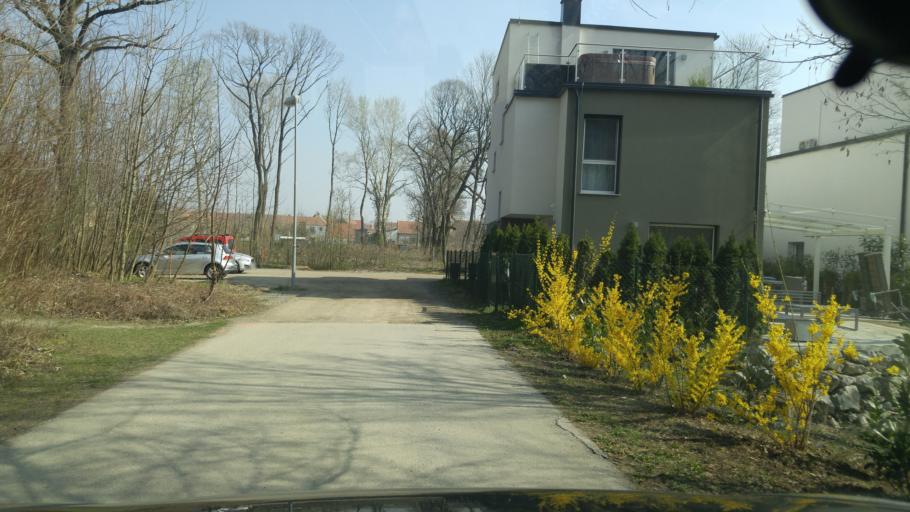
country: AT
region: Lower Austria
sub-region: Politischer Bezirk Wien-Umgebung
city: Moosbrunn
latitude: 48.0426
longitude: 16.4400
